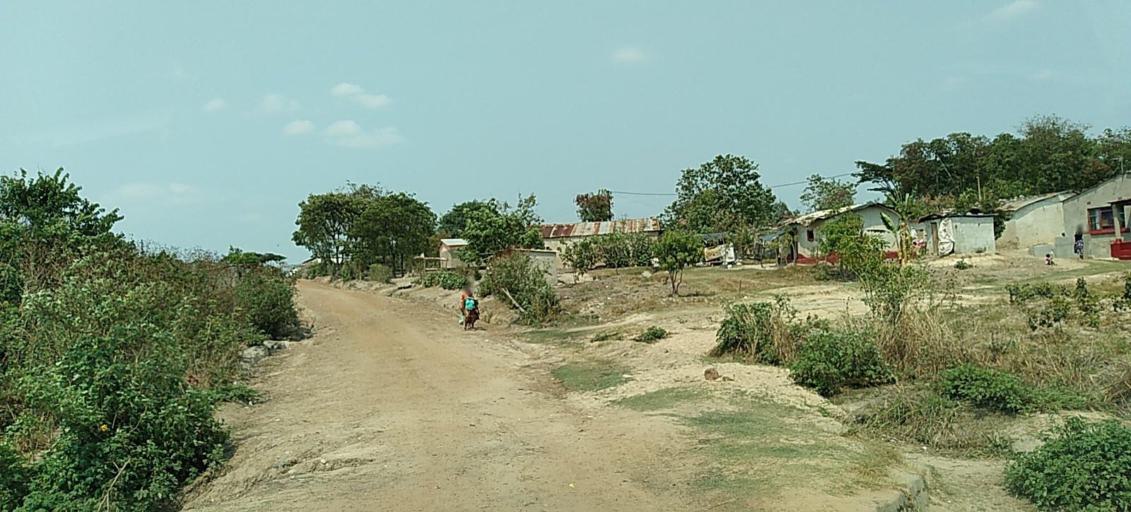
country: ZM
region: Copperbelt
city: Chambishi
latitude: -12.6253
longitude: 28.0798
